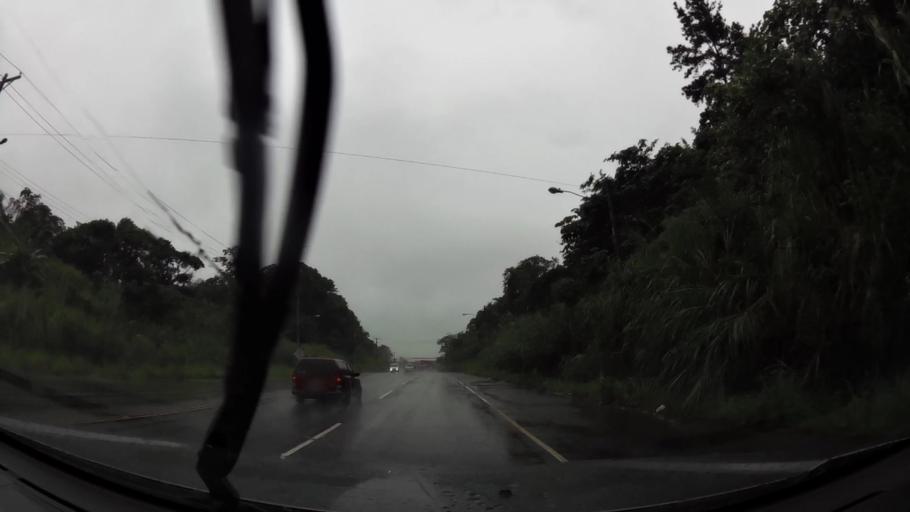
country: PA
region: Colon
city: Santa Rita Arriba
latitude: 9.3280
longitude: -79.8009
